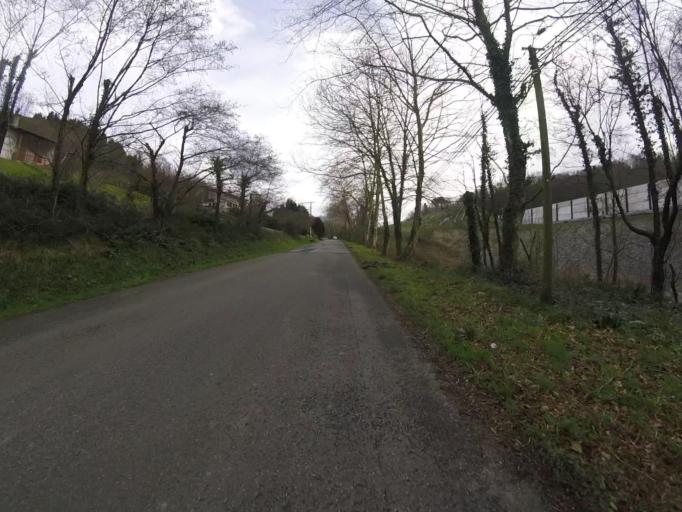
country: FR
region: Aquitaine
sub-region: Departement des Pyrenees-Atlantiques
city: Urrugne
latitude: 43.3415
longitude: -1.7321
